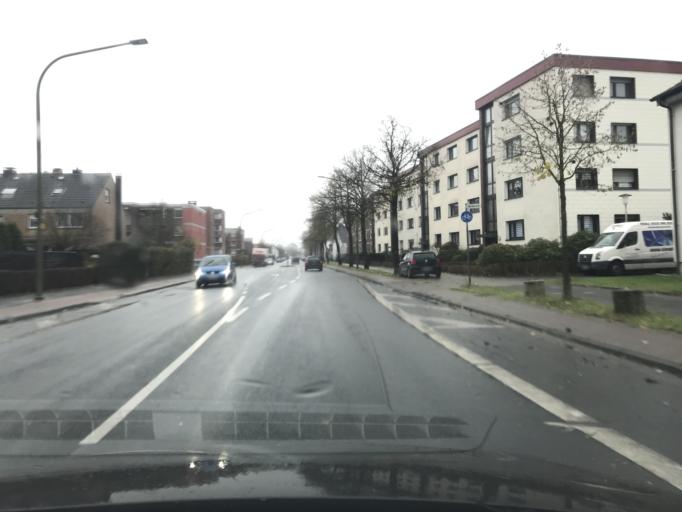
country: DE
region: North Rhine-Westphalia
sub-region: Regierungsbezirk Arnsberg
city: Hamm
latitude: 51.6910
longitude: 7.8706
